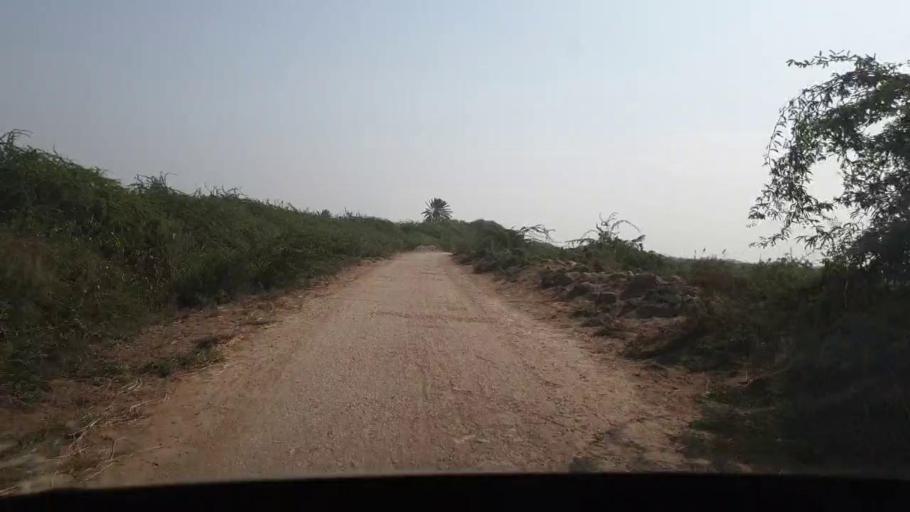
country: PK
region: Sindh
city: Chuhar Jamali
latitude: 24.2524
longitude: 67.9880
